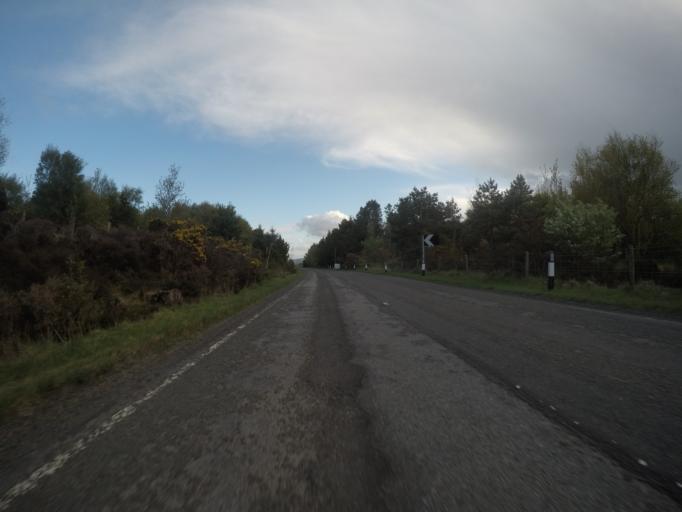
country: GB
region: Scotland
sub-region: Highland
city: Portree
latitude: 57.5703
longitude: -6.3644
